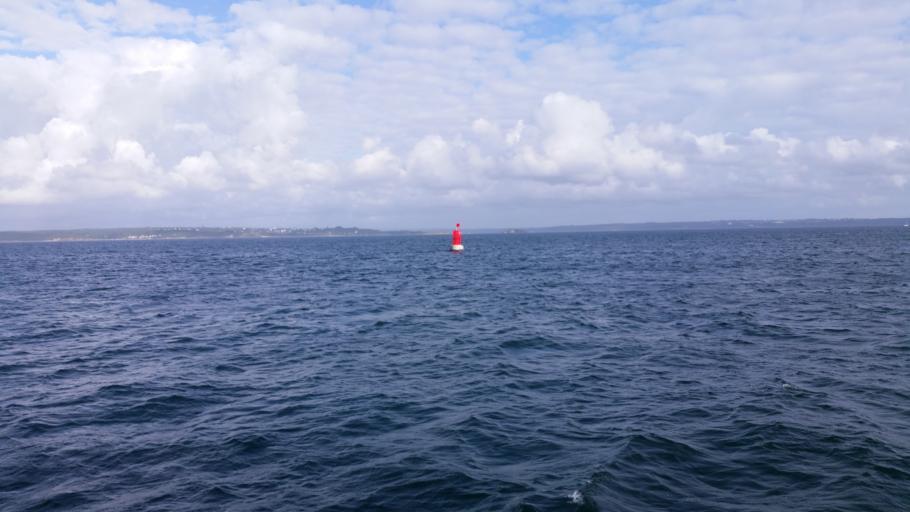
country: FR
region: Brittany
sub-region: Departement du Finistere
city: Brest
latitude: 48.3586
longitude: -4.5082
